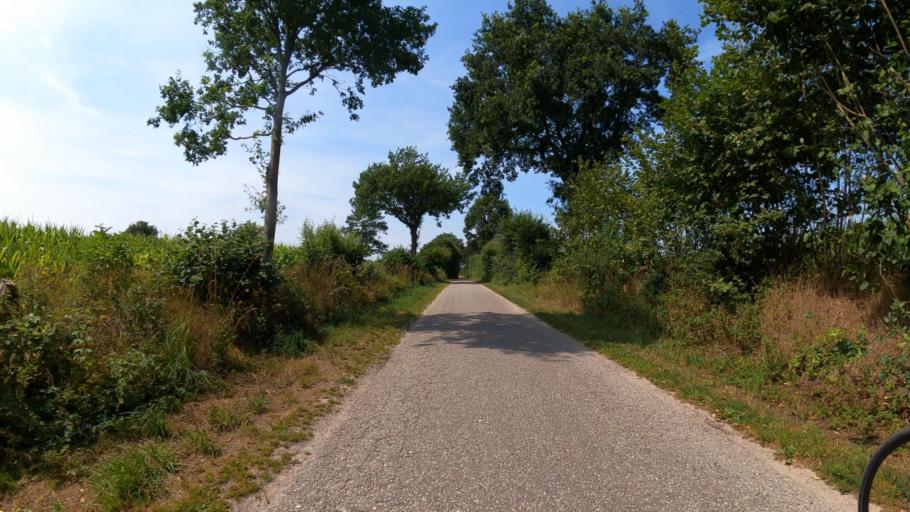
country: DE
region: Schleswig-Holstein
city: Seth
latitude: 53.8472
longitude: 10.1673
